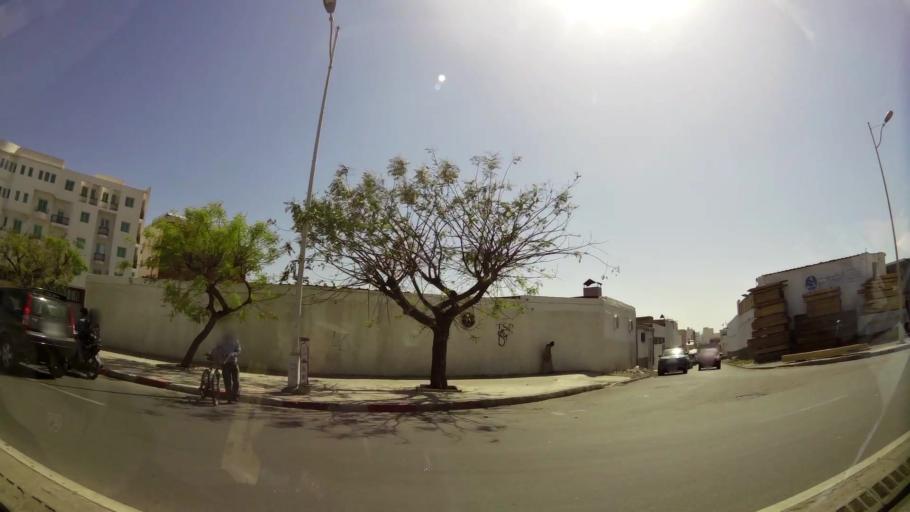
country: MA
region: Oued ed Dahab-Lagouira
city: Dakhla
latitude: 30.4171
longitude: -9.5743
